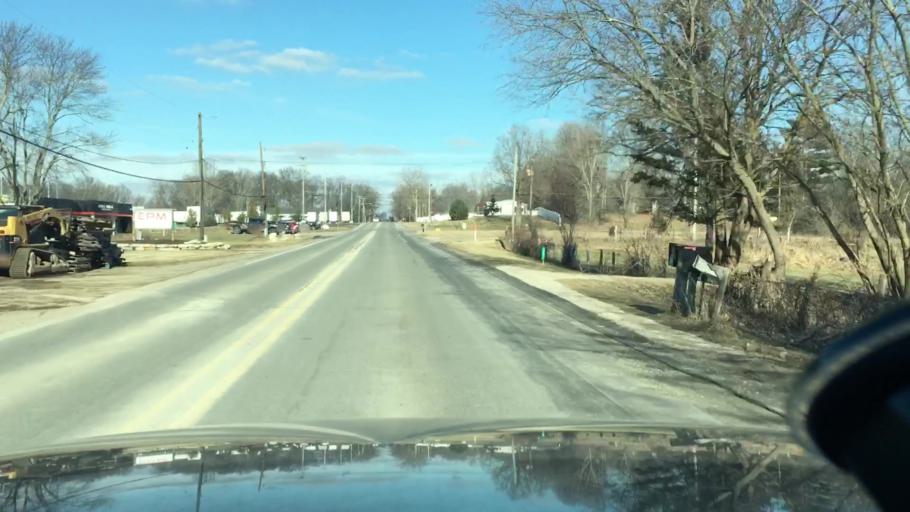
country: US
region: Michigan
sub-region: Jackson County
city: Jackson
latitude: 42.2825
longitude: -84.4303
